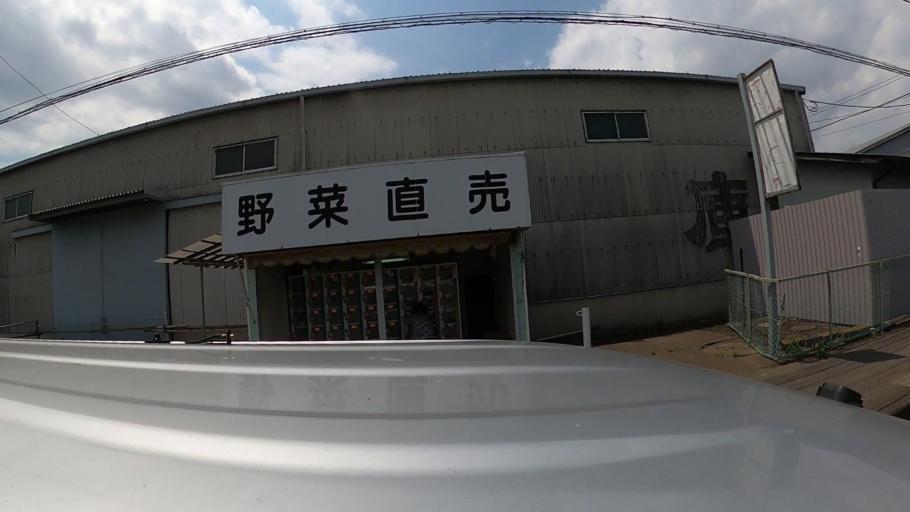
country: JP
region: Kanagawa
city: Chigasaki
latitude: 35.3862
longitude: 139.4019
